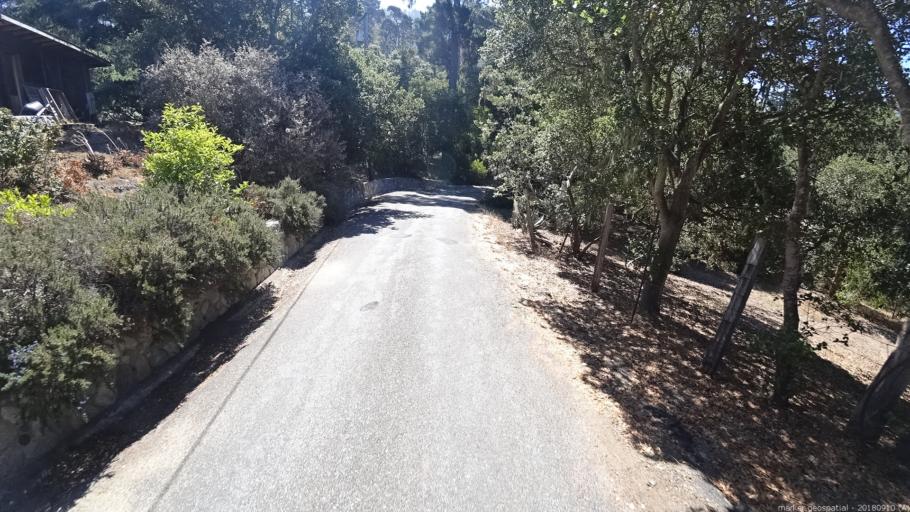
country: US
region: California
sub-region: Monterey County
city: Carmel-by-the-Sea
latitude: 36.5059
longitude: -121.9340
